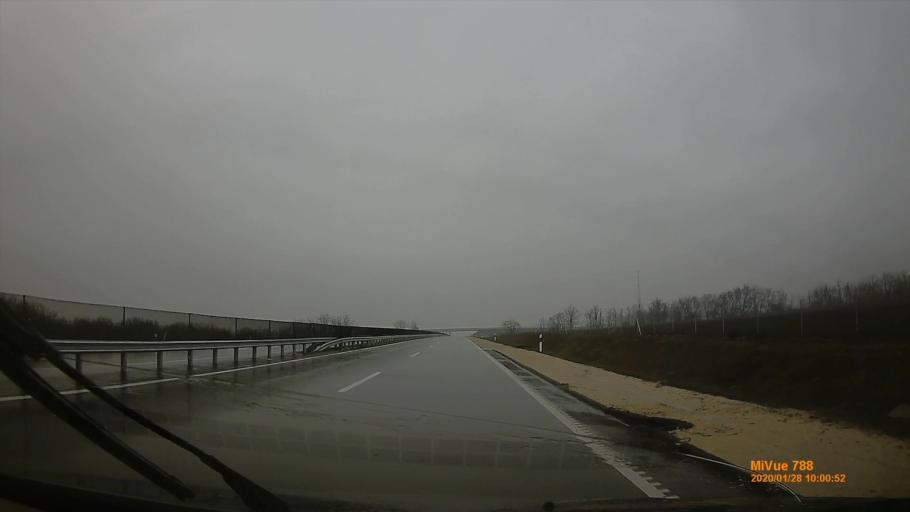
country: HU
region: Pest
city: Albertirsa
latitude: 47.2675
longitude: 19.6109
